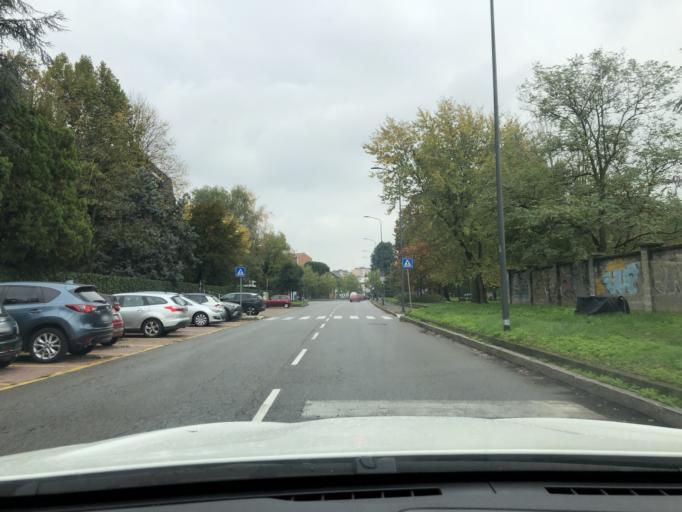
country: IT
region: Lombardy
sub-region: Citta metropolitana di Milano
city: Figino
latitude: 45.4777
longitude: 9.1153
